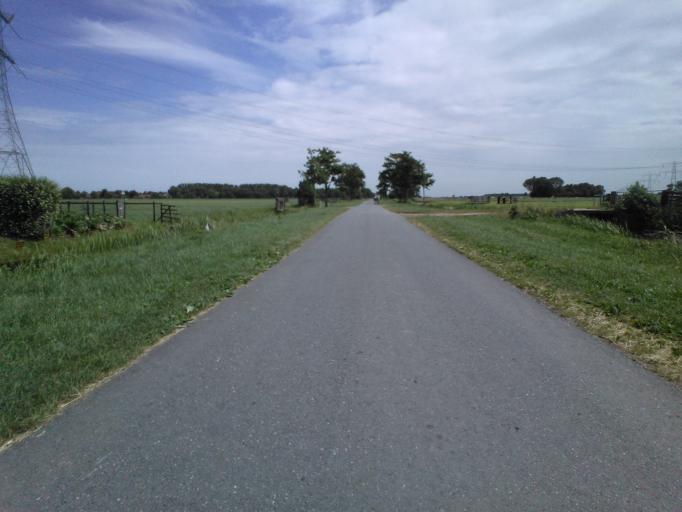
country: NL
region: South Holland
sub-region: Molenwaard
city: Nieuw-Lekkerland
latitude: 51.8810
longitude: 4.6796
